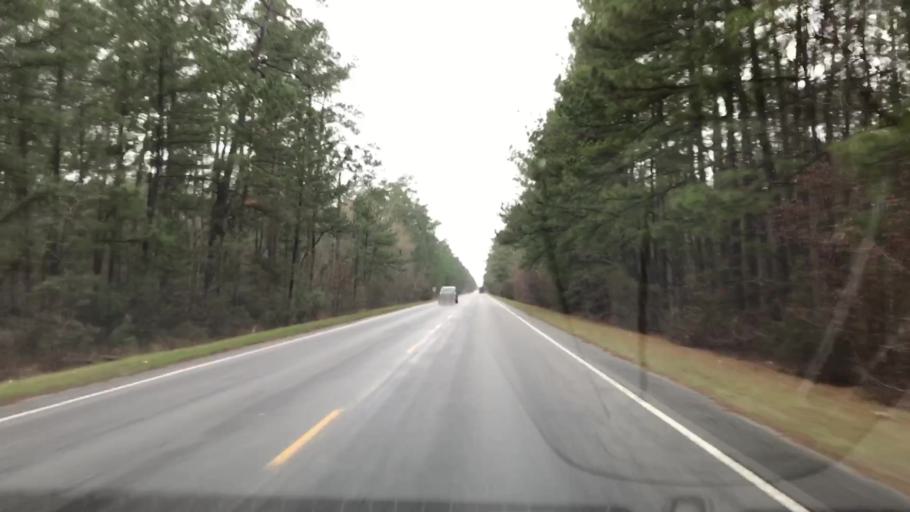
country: US
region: South Carolina
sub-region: Berkeley County
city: Saint Stephen
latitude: 33.2881
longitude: -79.8276
